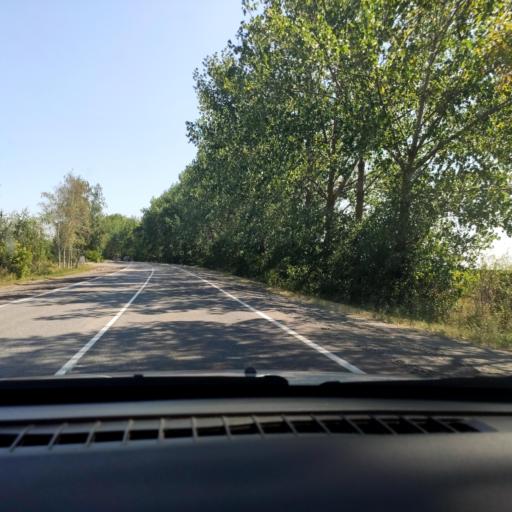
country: RU
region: Voronezj
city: Ostrogozhsk
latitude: 50.8234
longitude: 39.1539
